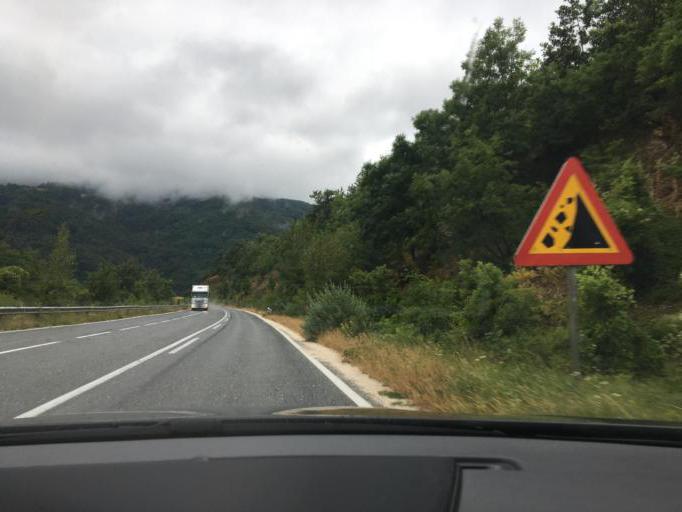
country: MK
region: Kriva Palanka
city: Kriva Palanka
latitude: 42.2210
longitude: 22.4415
